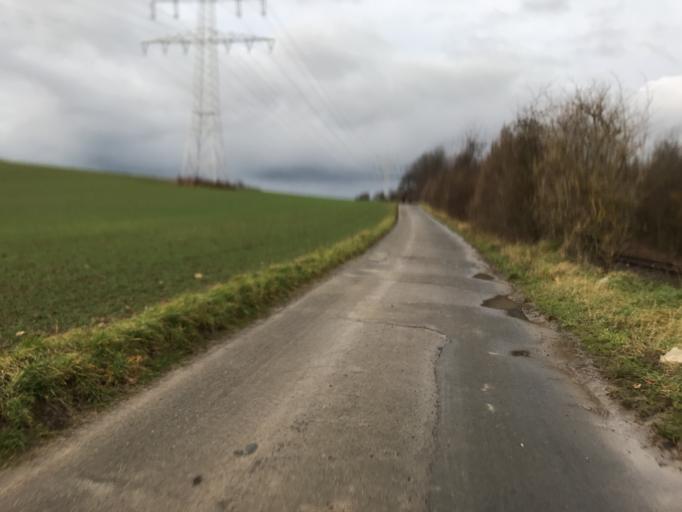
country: DE
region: Rheinland-Pfalz
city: Klein-Winternheim
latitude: 49.9679
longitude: 8.2204
